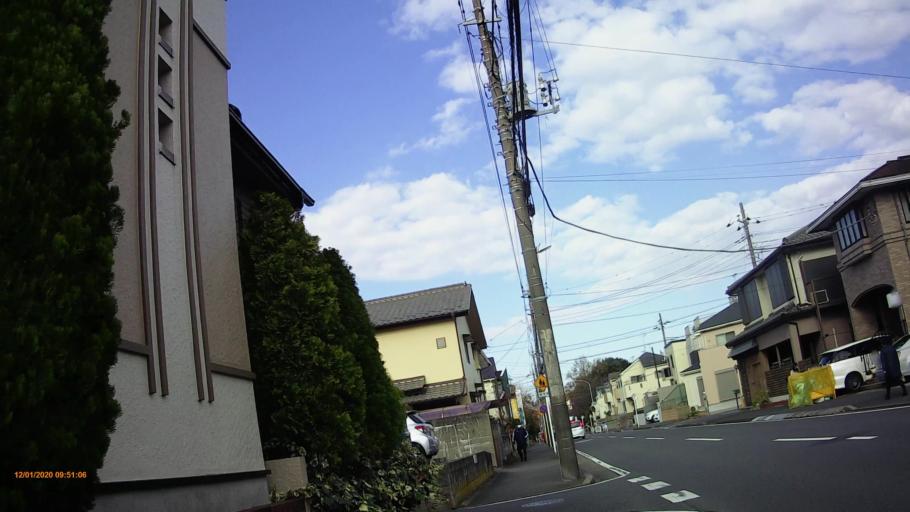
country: JP
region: Chiba
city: Yotsukaido
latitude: 35.6242
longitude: 140.1908
